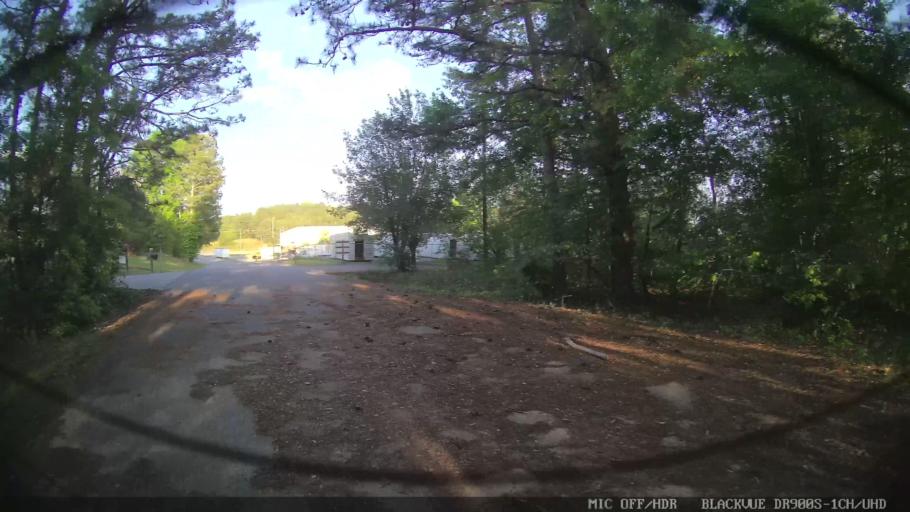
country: US
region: Georgia
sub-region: Bartow County
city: Cartersville
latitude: 34.1444
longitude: -84.8011
